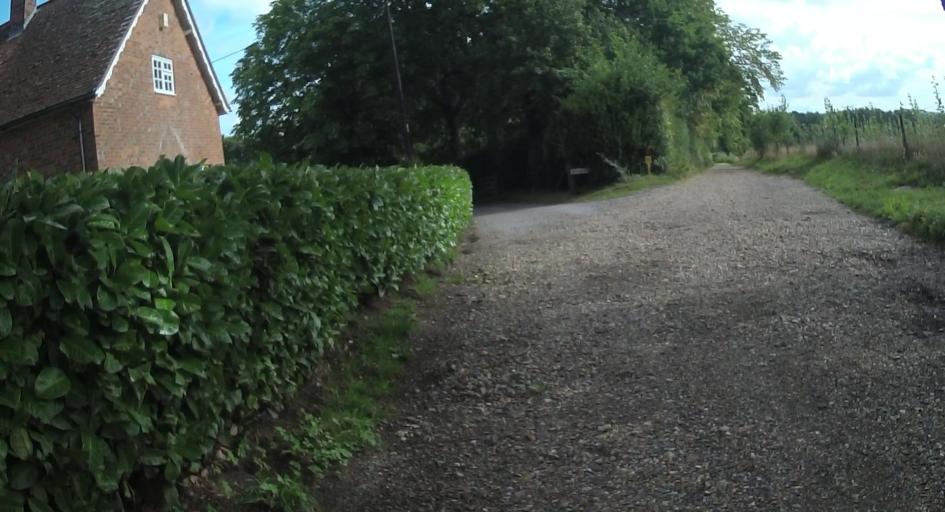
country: GB
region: England
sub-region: Hampshire
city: Kingsclere
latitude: 51.3716
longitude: -1.2086
